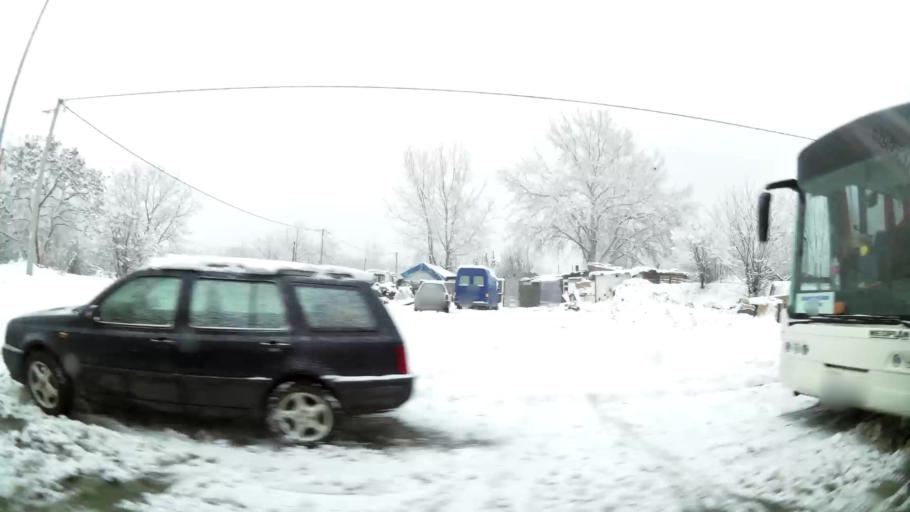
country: RS
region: Central Serbia
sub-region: Belgrade
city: Novi Beograd
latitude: 44.7995
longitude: 20.4046
